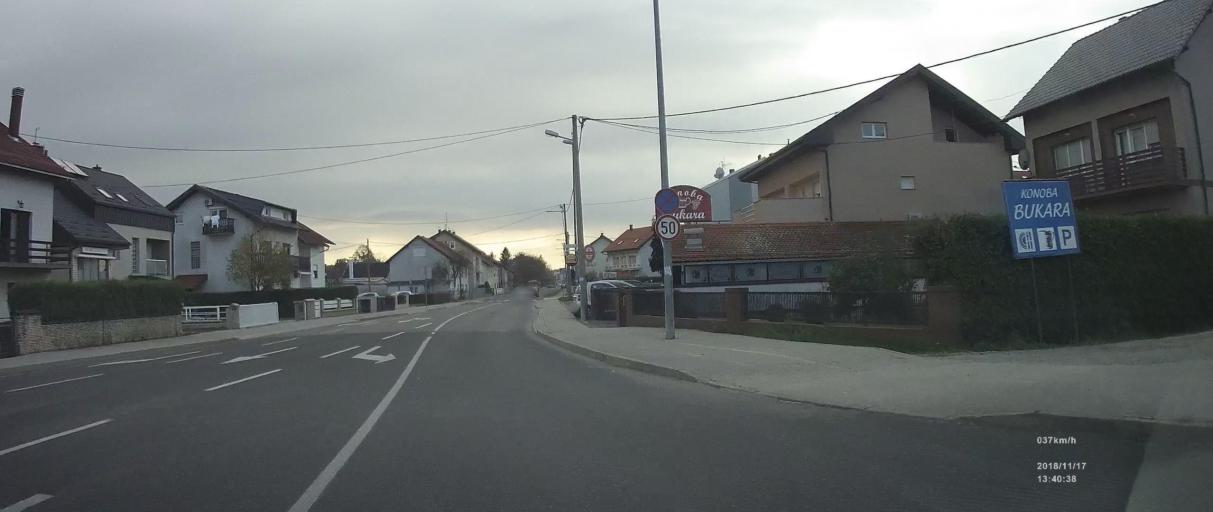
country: HR
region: Zagrebacka
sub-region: Grad Velika Gorica
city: Velika Gorica
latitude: 45.7227
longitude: 16.0705
